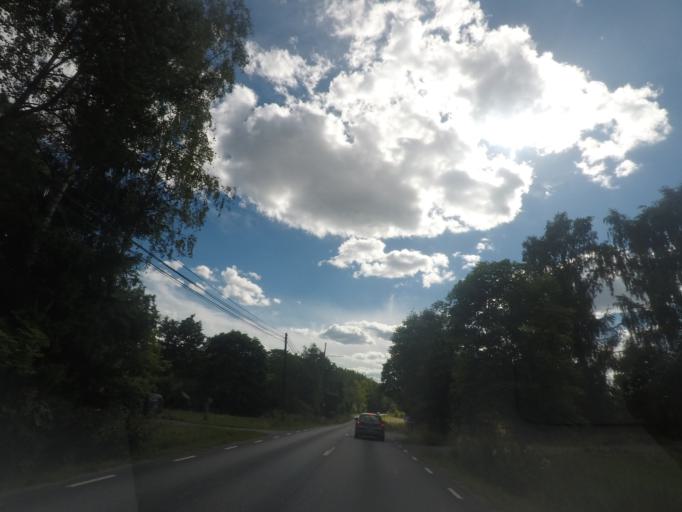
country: SE
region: Stockholm
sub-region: Norrtalje Kommun
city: Arno
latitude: 60.0817
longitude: 18.7832
